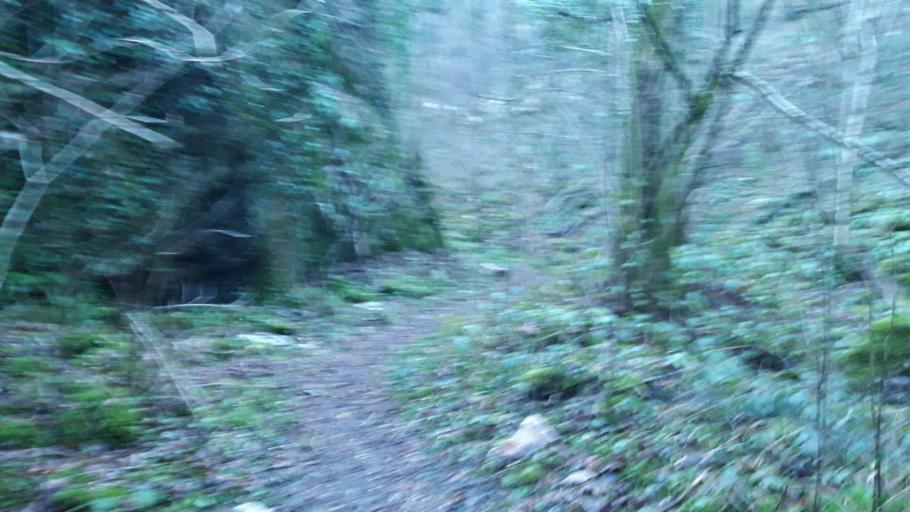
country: FR
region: Rhone-Alpes
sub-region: Departement de l'Isere
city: Seyssins
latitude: 45.1755
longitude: 5.6704
